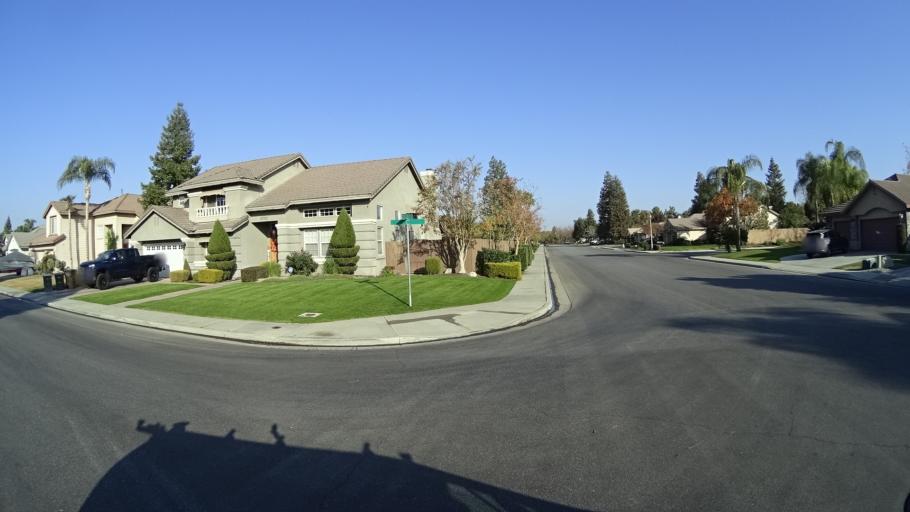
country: US
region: California
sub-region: Kern County
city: Greenacres
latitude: 35.3665
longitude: -119.1209
